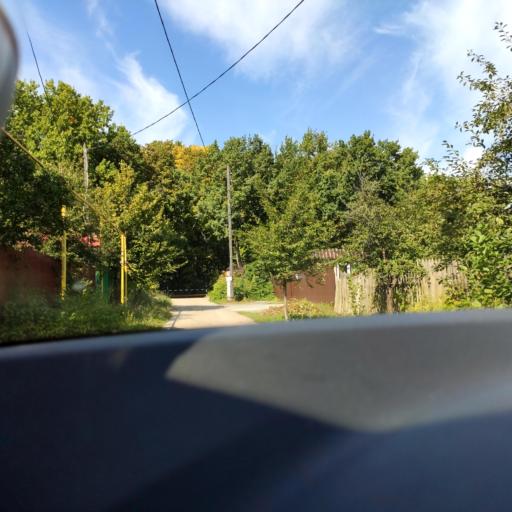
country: RU
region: Samara
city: Samara
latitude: 53.2949
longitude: 50.2125
